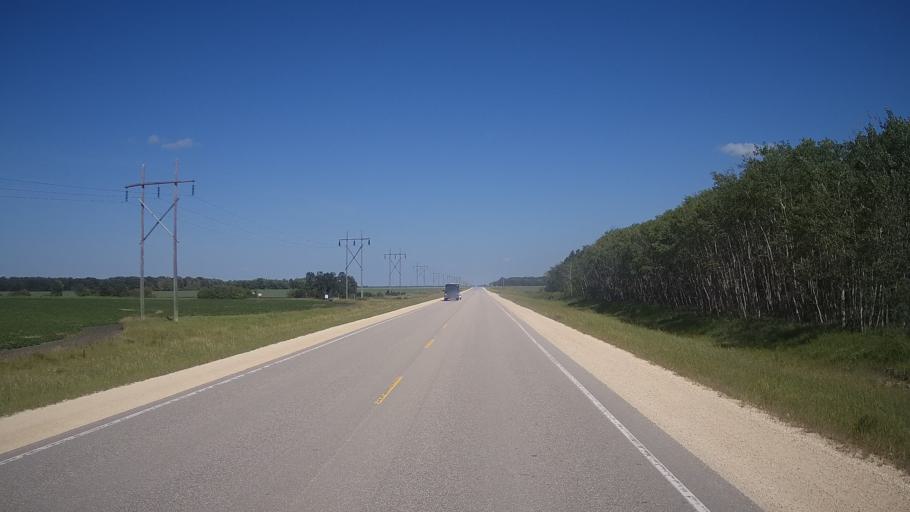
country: CA
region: Manitoba
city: Stonewall
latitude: 50.1227
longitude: -97.4515
